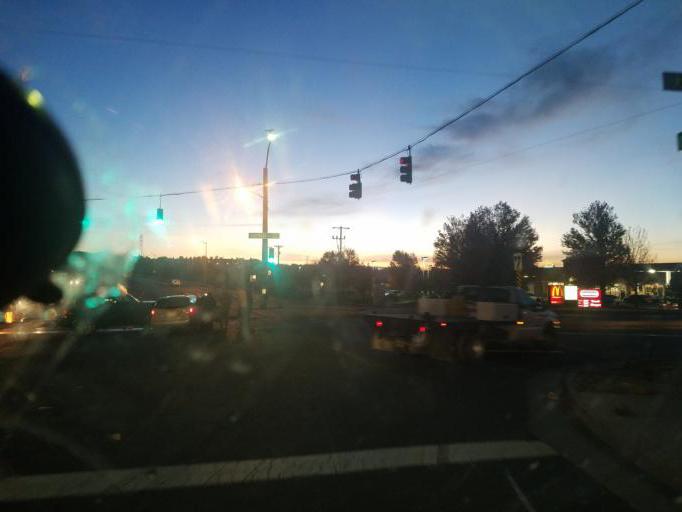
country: US
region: Colorado
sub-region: El Paso County
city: Stratmoor
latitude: 38.7957
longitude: -104.7903
